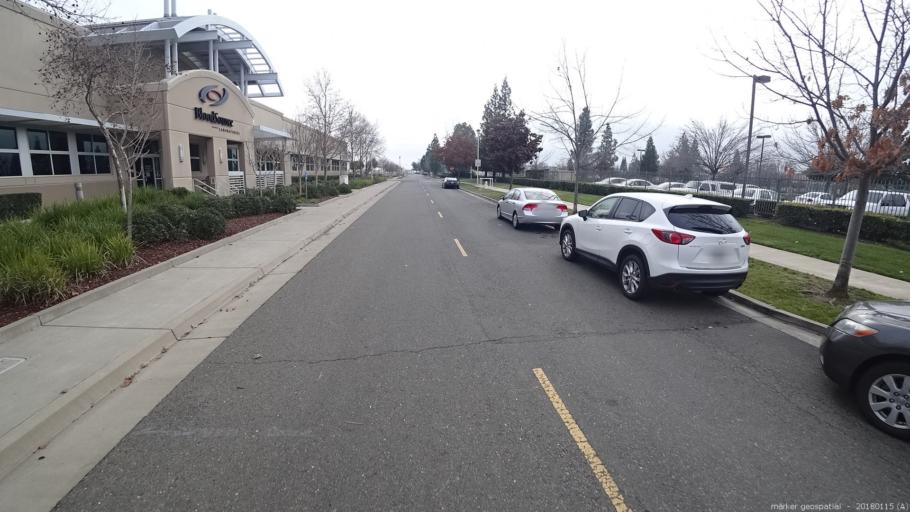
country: US
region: California
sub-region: Sacramento County
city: Rancho Cordova
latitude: 38.5698
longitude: -121.2949
